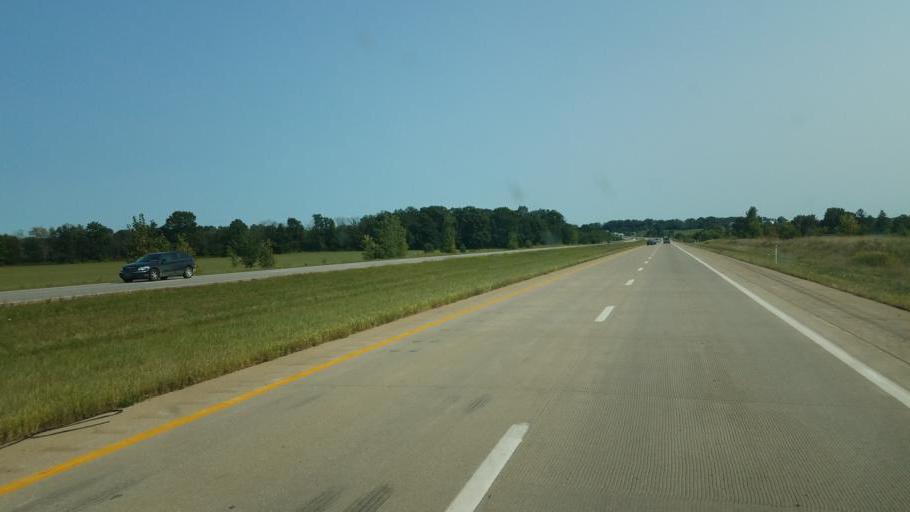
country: US
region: Ohio
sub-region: Wayne County
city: Apple Creek
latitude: 40.8013
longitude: -81.8189
